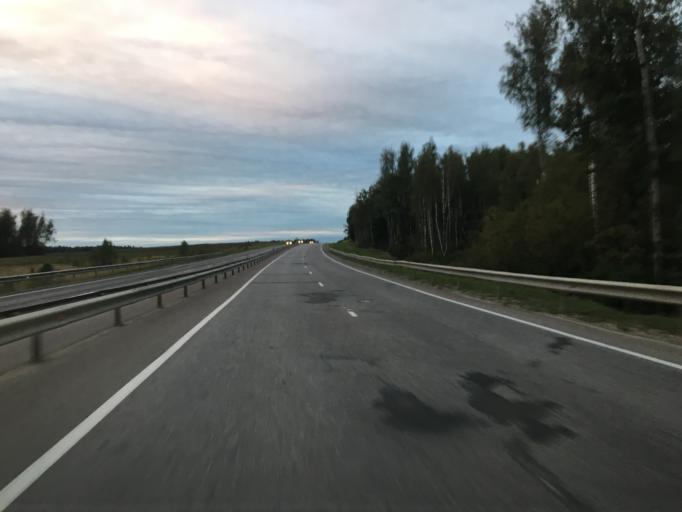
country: RU
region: Kaluga
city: Kaluga
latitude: 54.6469
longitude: 36.2940
